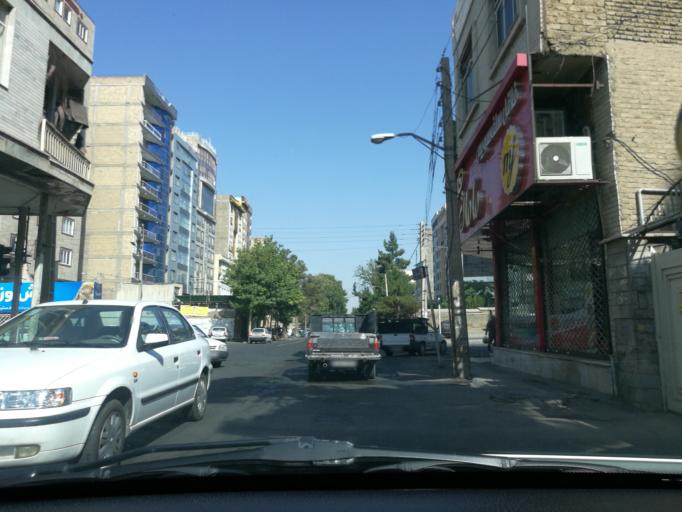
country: IR
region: Alborz
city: Karaj
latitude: 35.8554
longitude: 50.9560
